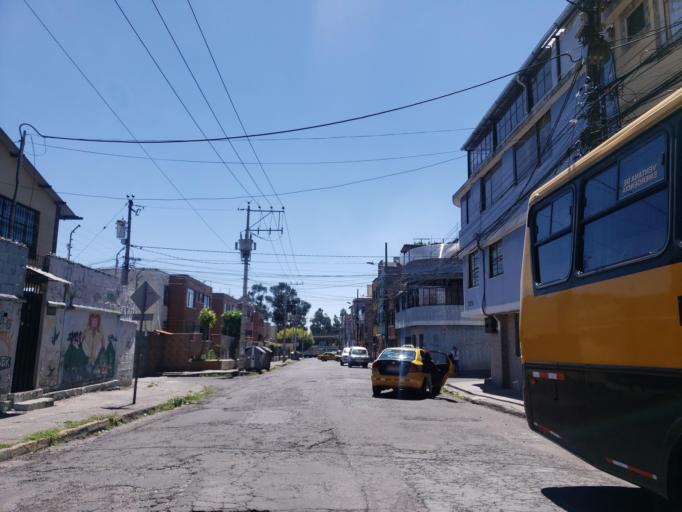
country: EC
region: Pichincha
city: Quito
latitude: -0.2645
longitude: -78.5384
